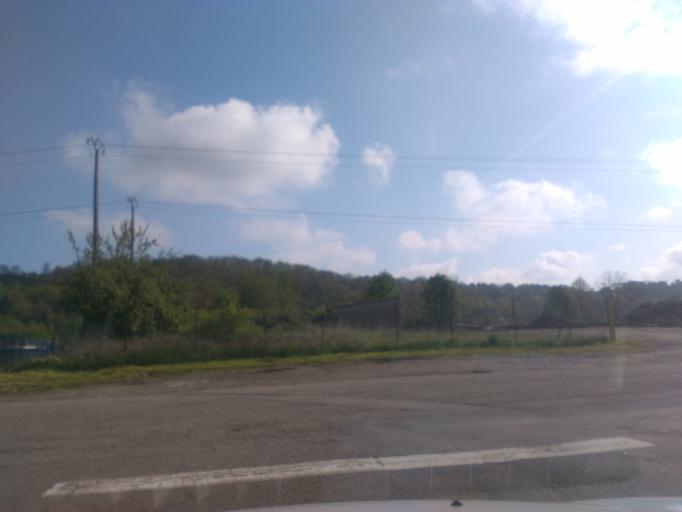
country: FR
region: Lorraine
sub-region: Departement des Vosges
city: Mirecourt
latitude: 48.3113
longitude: 6.1354
